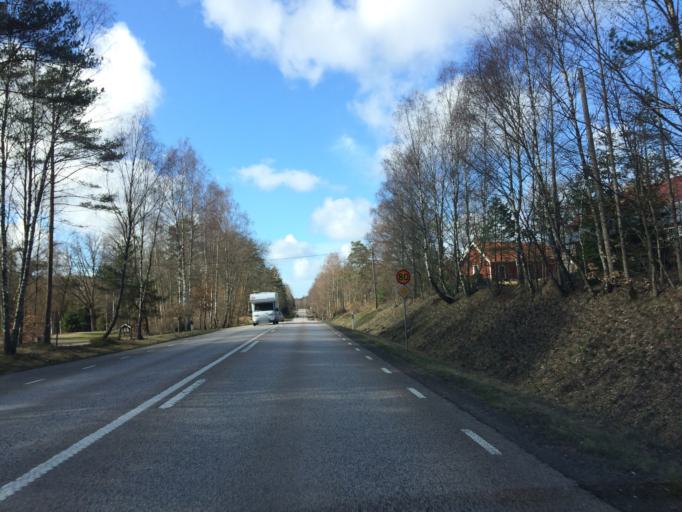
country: SE
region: Kronoberg
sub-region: Markaryds Kommun
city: Markaryd
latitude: 56.4926
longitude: 13.4636
